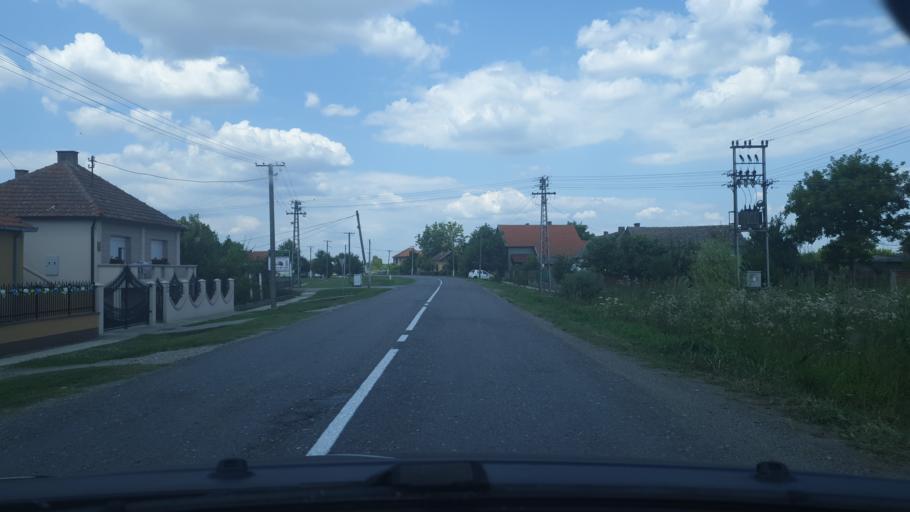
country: RS
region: Autonomna Pokrajina Vojvodina
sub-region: Sremski Okrug
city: Pecinci
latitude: 44.8478
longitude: 19.9617
